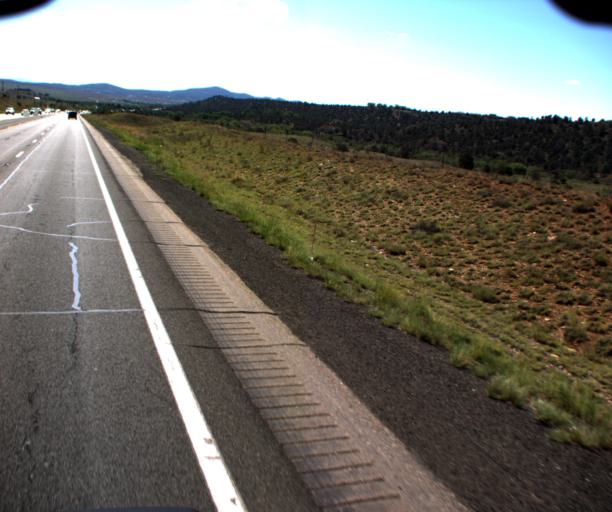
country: US
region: Arizona
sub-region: Yavapai County
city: Prescott Valley
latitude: 34.5759
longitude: -112.2871
